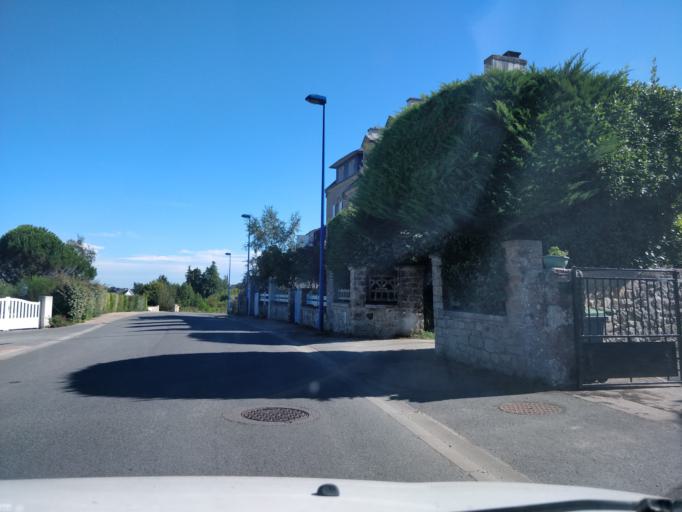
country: FR
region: Brittany
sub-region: Departement du Morbihan
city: Locmariaquer
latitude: 47.5730
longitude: -2.9493
